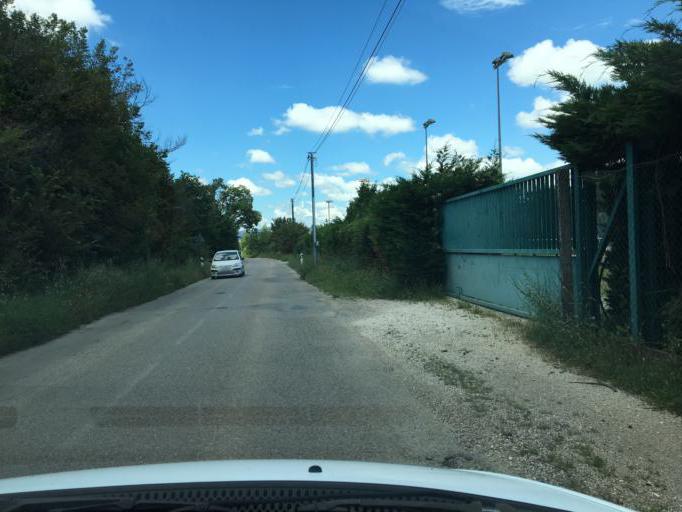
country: FR
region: Provence-Alpes-Cote d'Azur
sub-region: Departement du Vaucluse
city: Carpentras
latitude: 44.0392
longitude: 5.0560
